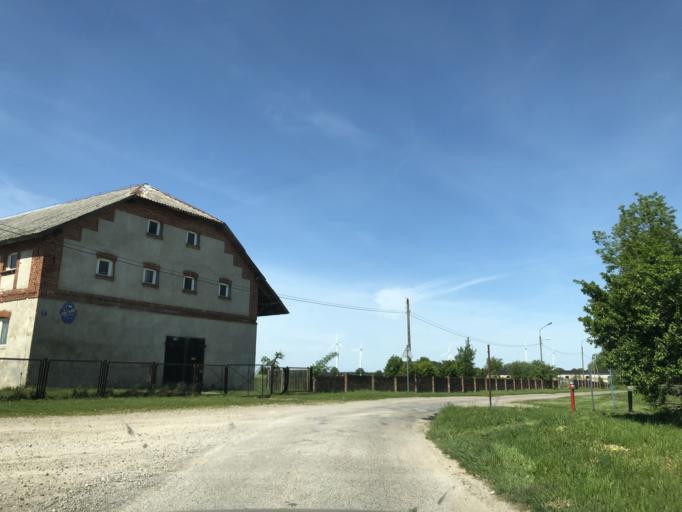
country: PL
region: West Pomeranian Voivodeship
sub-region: Powiat kolobrzeski
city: Goscino
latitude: 54.0450
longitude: 15.7259
